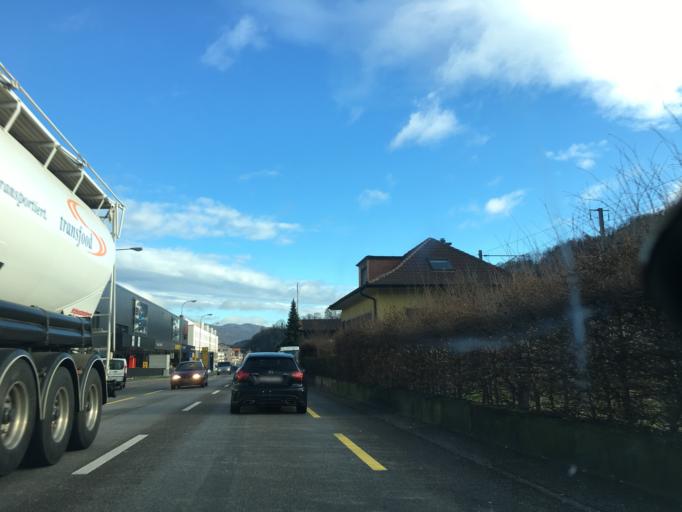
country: CH
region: Aargau
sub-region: Bezirk Zofingen
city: Aarburg
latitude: 47.3325
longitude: 7.9061
